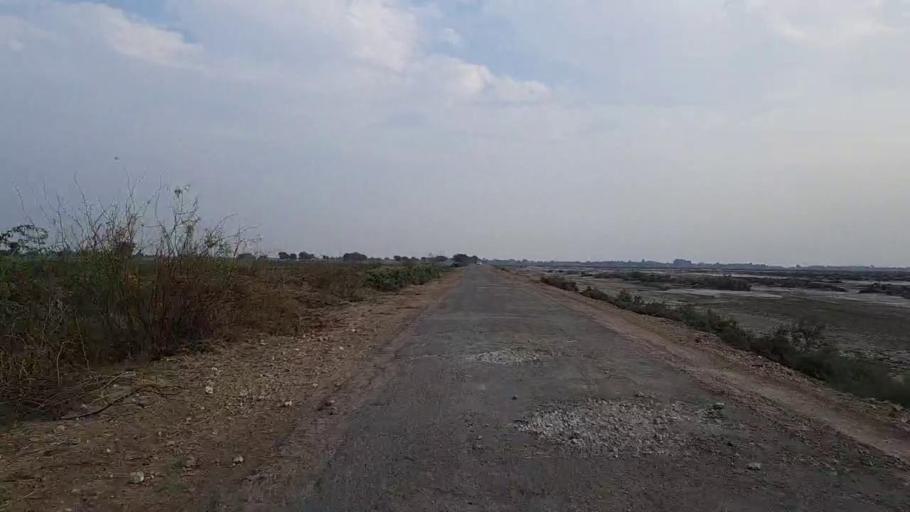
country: PK
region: Sindh
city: Pithoro
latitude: 25.4737
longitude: 69.2694
